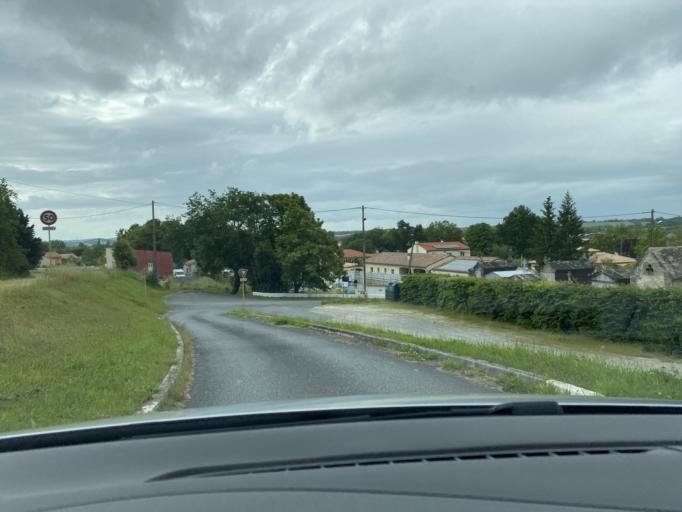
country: FR
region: Midi-Pyrenees
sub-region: Departement du Tarn
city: Saix
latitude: 43.5809
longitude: 2.1803
